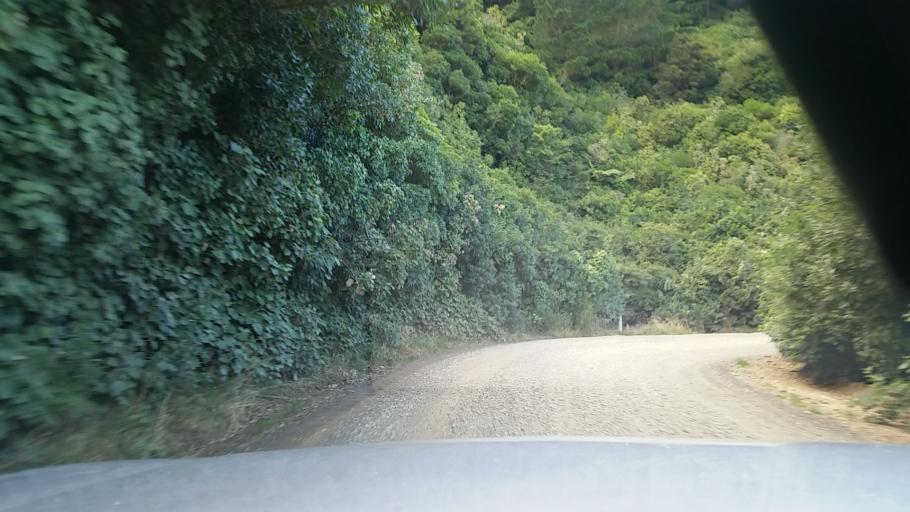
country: NZ
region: Marlborough
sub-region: Marlborough District
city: Picton
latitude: -41.2806
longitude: 174.1515
